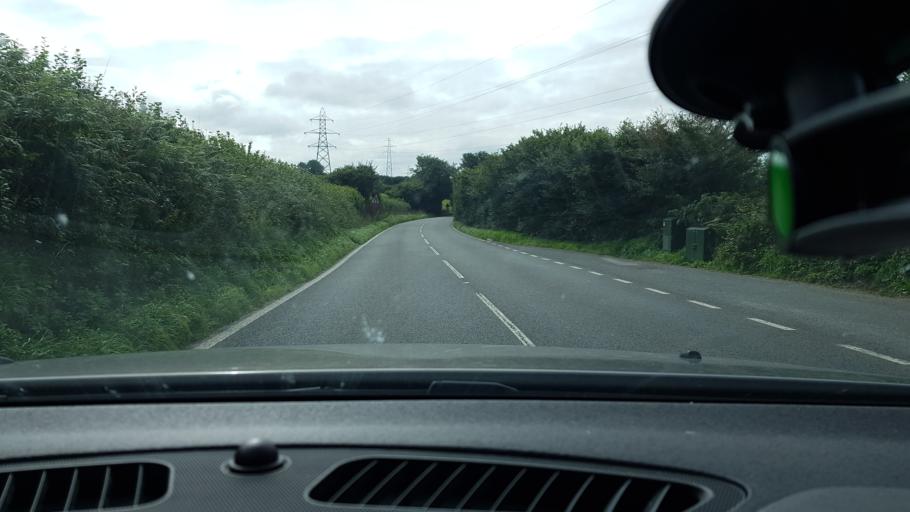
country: GB
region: England
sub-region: Cornwall
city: Camelford
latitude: 50.6038
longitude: -4.6950
